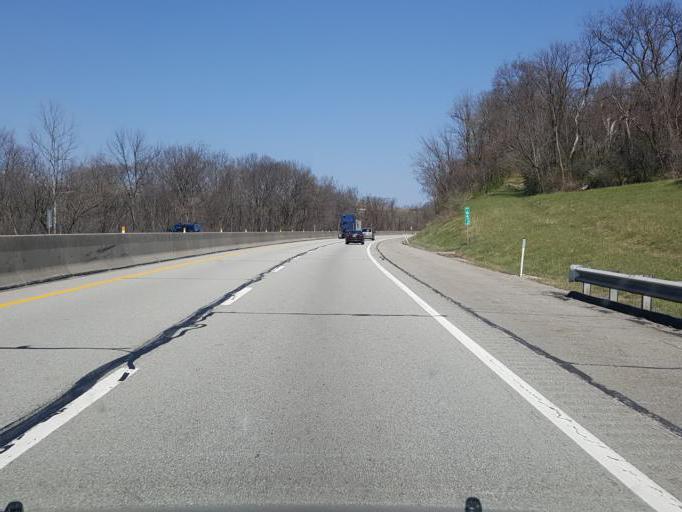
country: US
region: Pennsylvania
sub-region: Westmoreland County
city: Irwin
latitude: 40.3389
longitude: -79.6922
